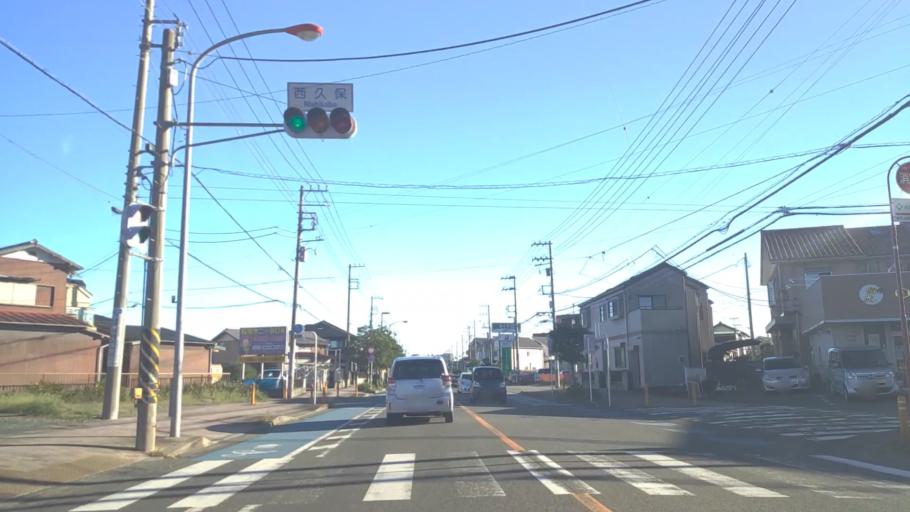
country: JP
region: Kanagawa
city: Chigasaki
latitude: 35.3484
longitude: 139.3972
